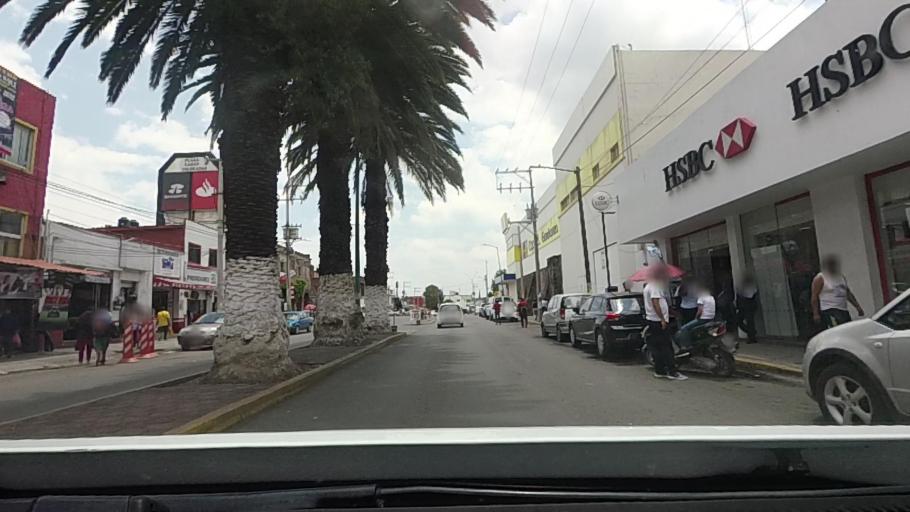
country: MX
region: Mexico
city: Chalco de Diaz Covarrubias
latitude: 19.2618
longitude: -98.8988
